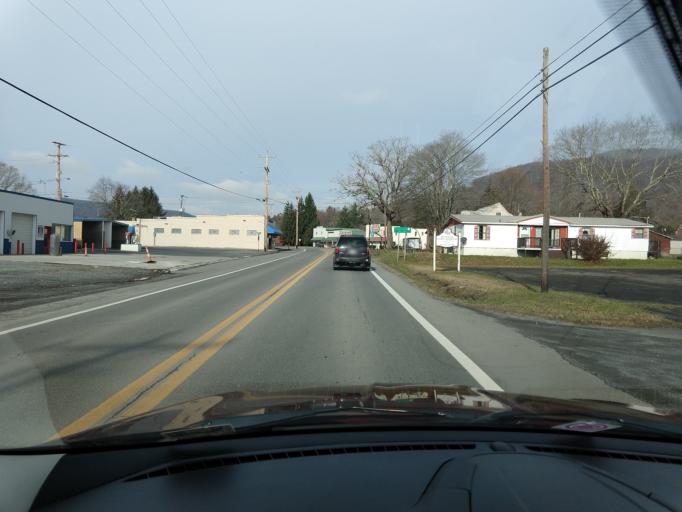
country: US
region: West Virginia
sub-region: Greenbrier County
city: Rainelle
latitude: 37.9622
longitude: -80.6870
